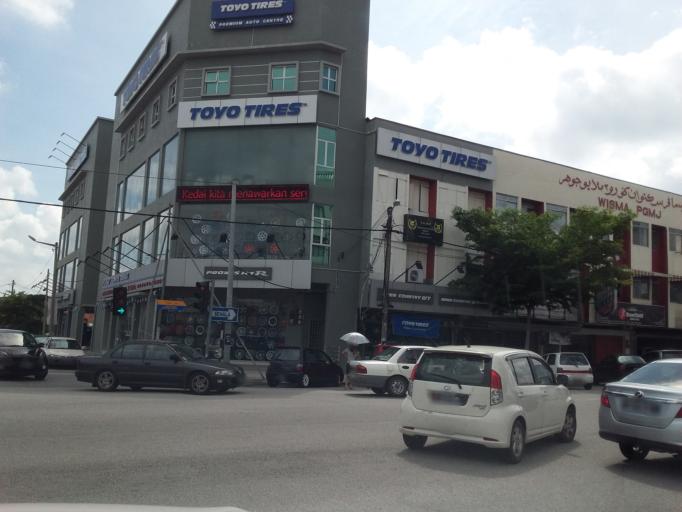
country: MY
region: Johor
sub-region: Daerah Batu Pahat
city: Batu Pahat
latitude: 1.8506
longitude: 102.9302
